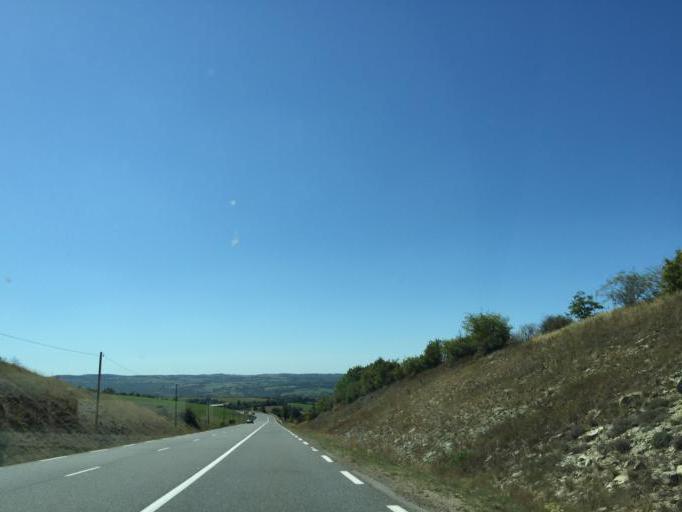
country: FR
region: Midi-Pyrenees
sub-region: Departement de l'Aveyron
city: Saint-Georges-de-Luzencon
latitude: 44.0142
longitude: 3.0237
